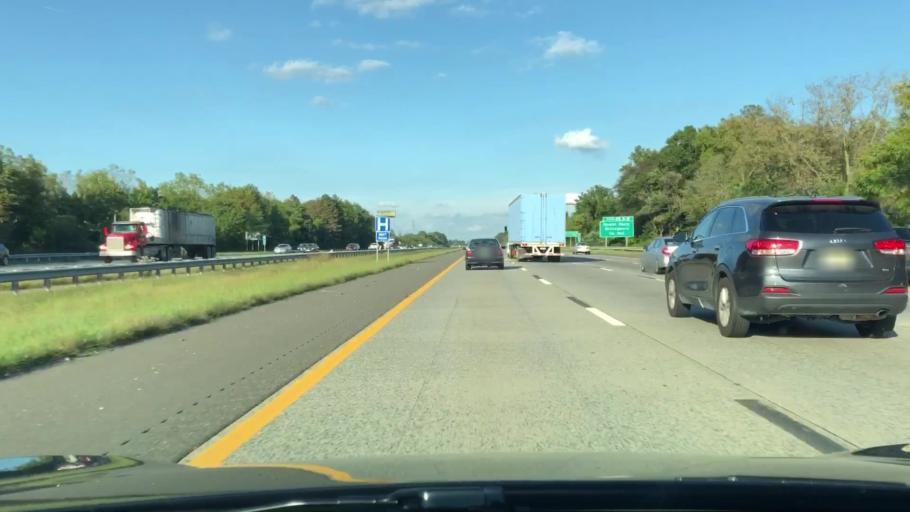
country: US
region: New Jersey
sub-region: Burlington County
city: Willingboro
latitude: 39.9983
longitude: -74.8646
